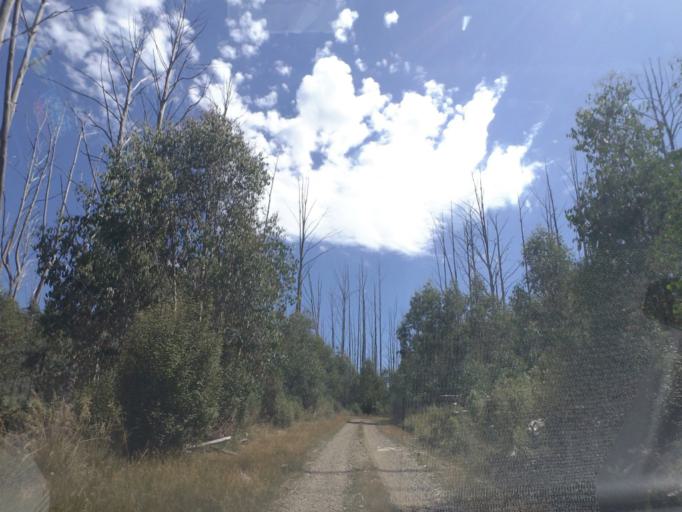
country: AU
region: Victoria
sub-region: Murrindindi
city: Alexandra
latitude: -37.4704
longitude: 145.8346
